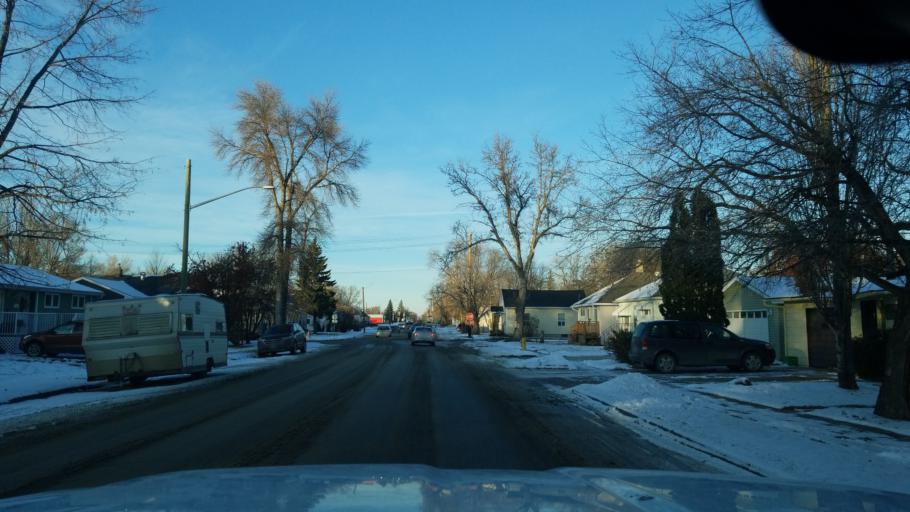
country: CA
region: Manitoba
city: Portage la Prairie
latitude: 49.9750
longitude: -98.3013
